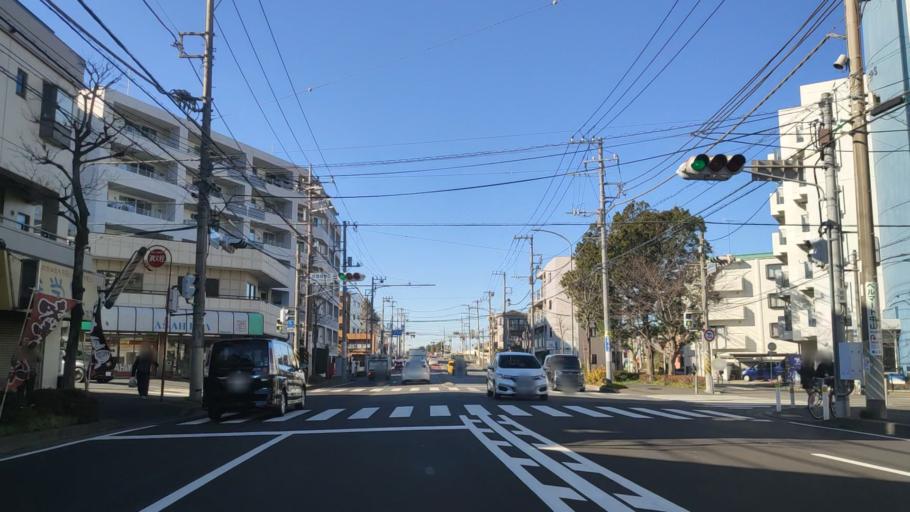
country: JP
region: Tokyo
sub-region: Machida-shi
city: Machida
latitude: 35.5155
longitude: 139.5356
